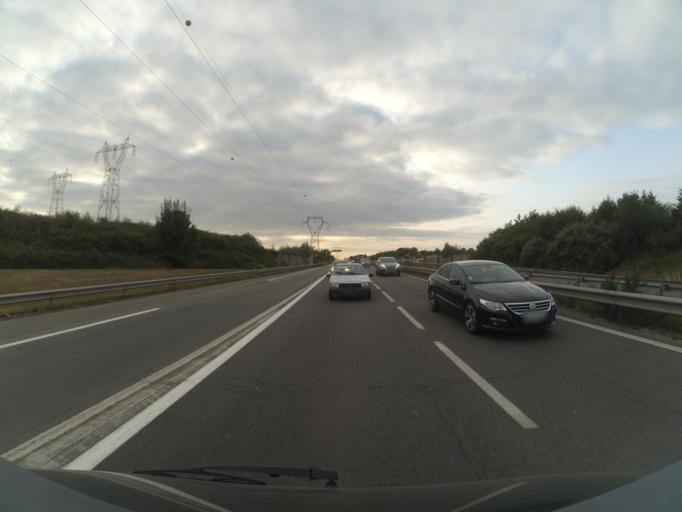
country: FR
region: Pays de la Loire
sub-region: Departement de la Loire-Atlantique
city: Reze
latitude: 47.1663
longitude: -1.5718
